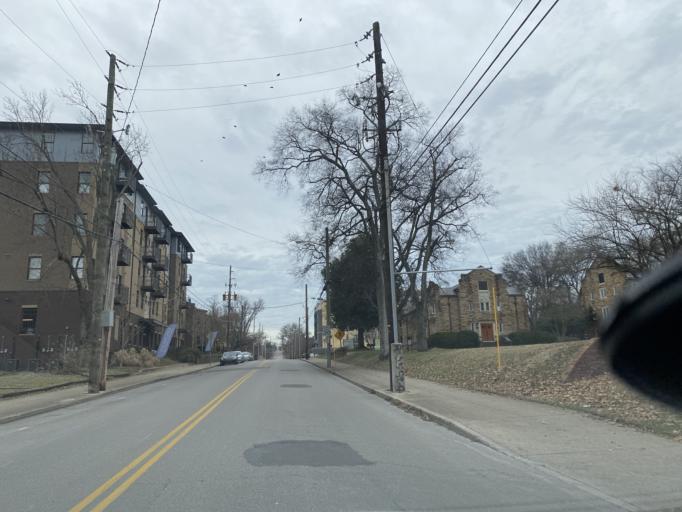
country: US
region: Tennessee
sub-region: Davidson County
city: Nashville
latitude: 36.1462
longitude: -86.7952
